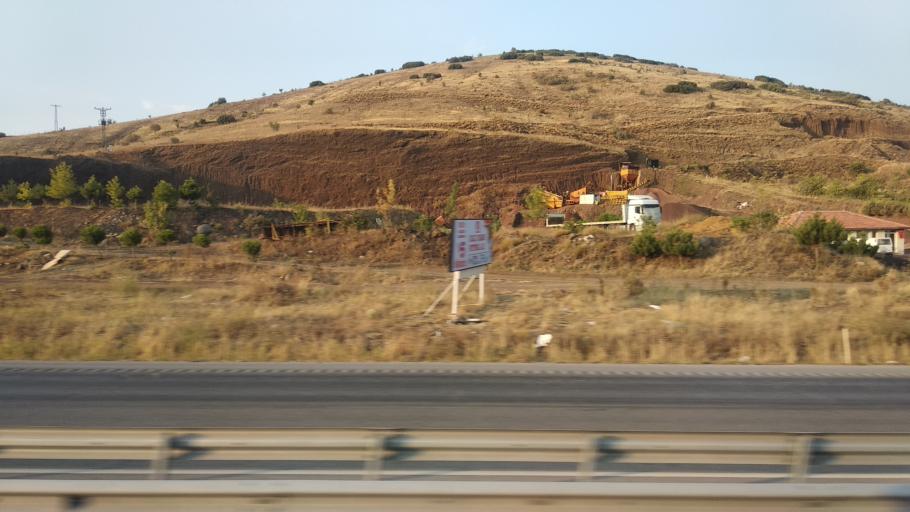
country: TR
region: Manisa
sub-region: Kula
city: Kula
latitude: 38.5671
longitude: 28.5814
